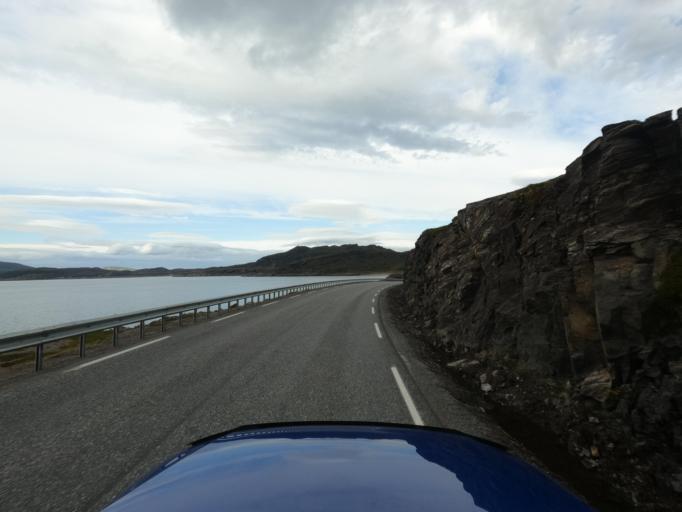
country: NO
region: Finnmark Fylke
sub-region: Hammerfest
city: Rypefjord
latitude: 70.5888
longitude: 23.6807
